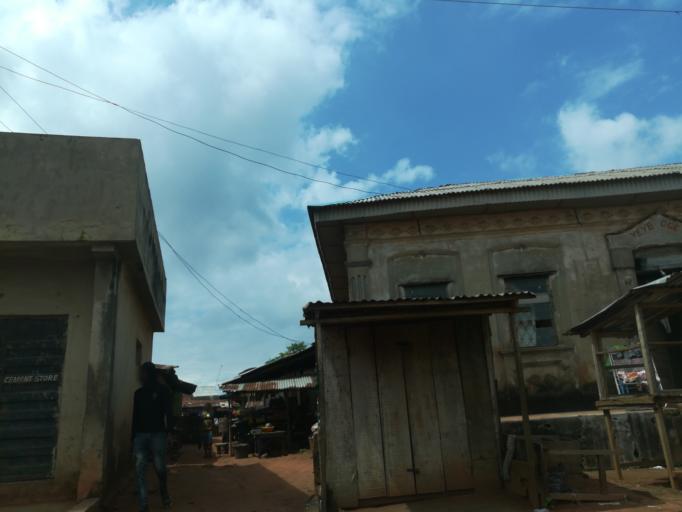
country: NG
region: Lagos
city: Ejirin
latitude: 6.6443
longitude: 3.7131
